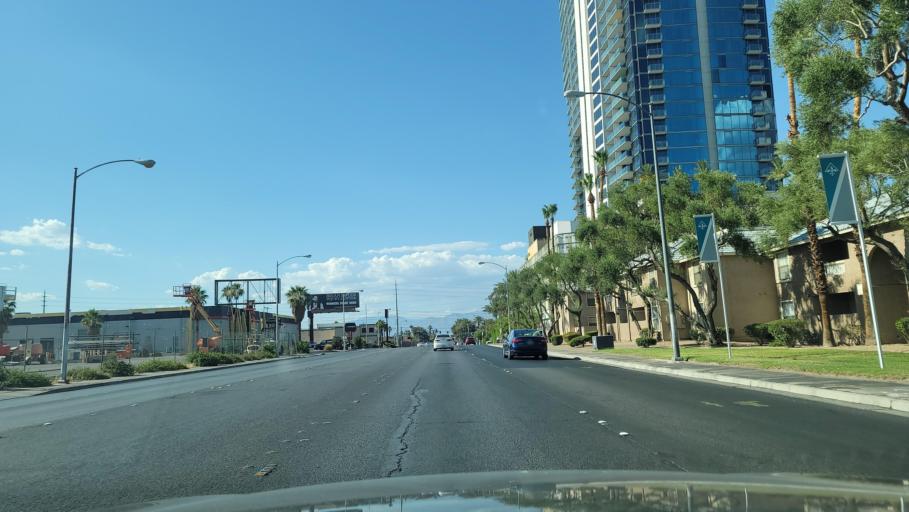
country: US
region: Nevada
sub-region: Clark County
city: Spring Valley
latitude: 36.1127
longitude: -115.1994
